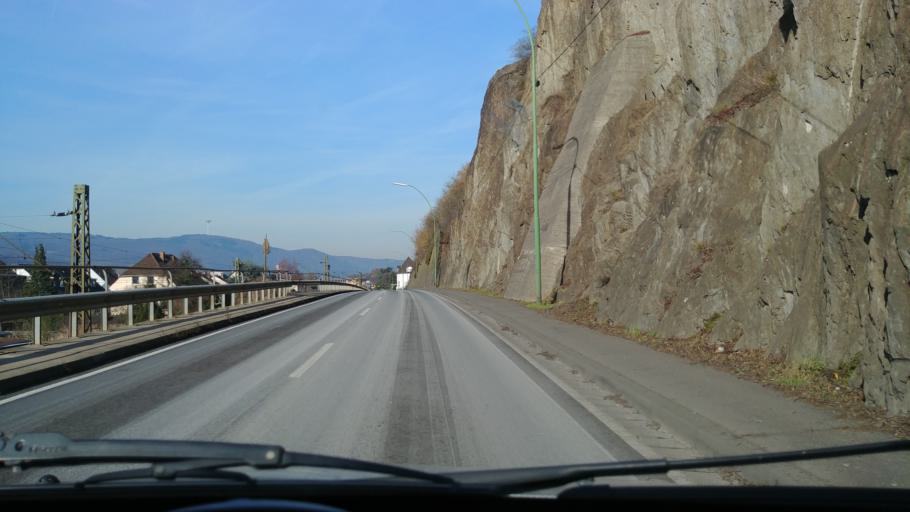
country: DE
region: Rheinland-Pfalz
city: Braubach
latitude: 50.2789
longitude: 7.6388
